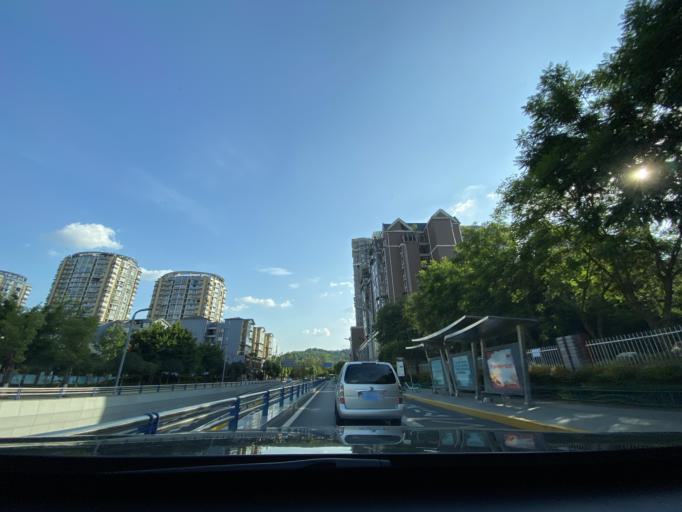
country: CN
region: Sichuan
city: Jiancheng
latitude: 30.4101
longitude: 104.5374
